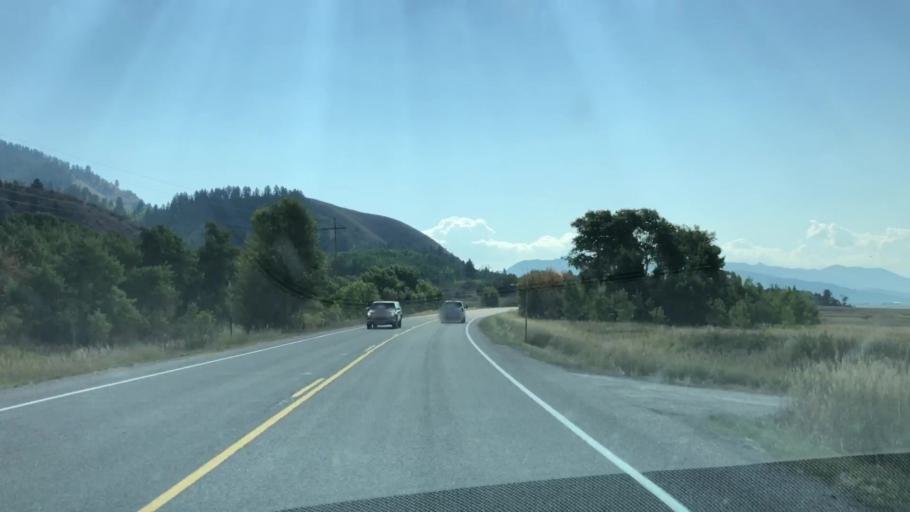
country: US
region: Wyoming
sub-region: Teton County
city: Hoback
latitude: 43.2159
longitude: -111.0641
